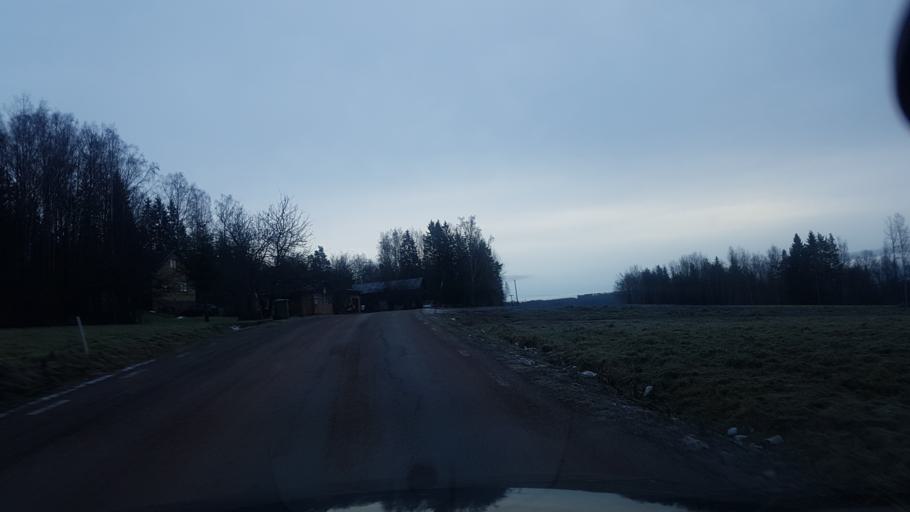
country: SE
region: Dalarna
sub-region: Borlange Kommun
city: Ornas
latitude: 60.4374
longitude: 15.6516
